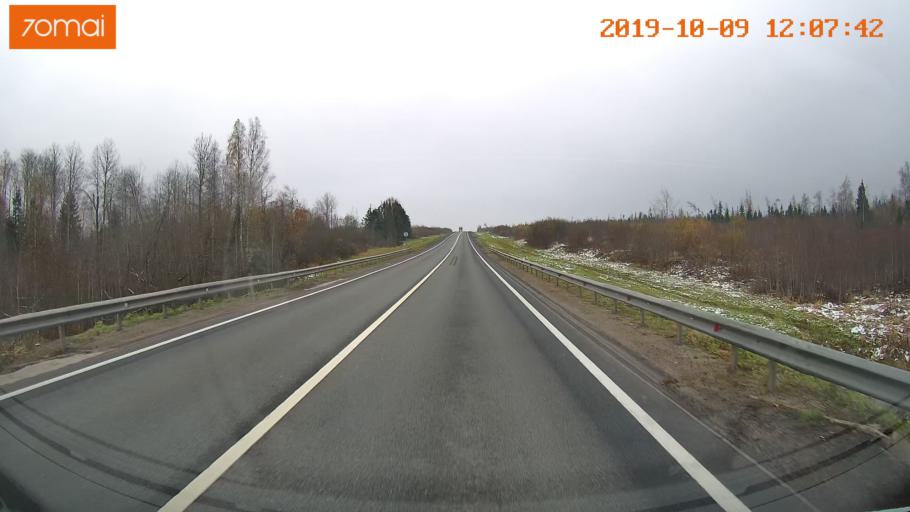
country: RU
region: Jaroslavl
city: Prechistoye
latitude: 58.5960
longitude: 40.3434
